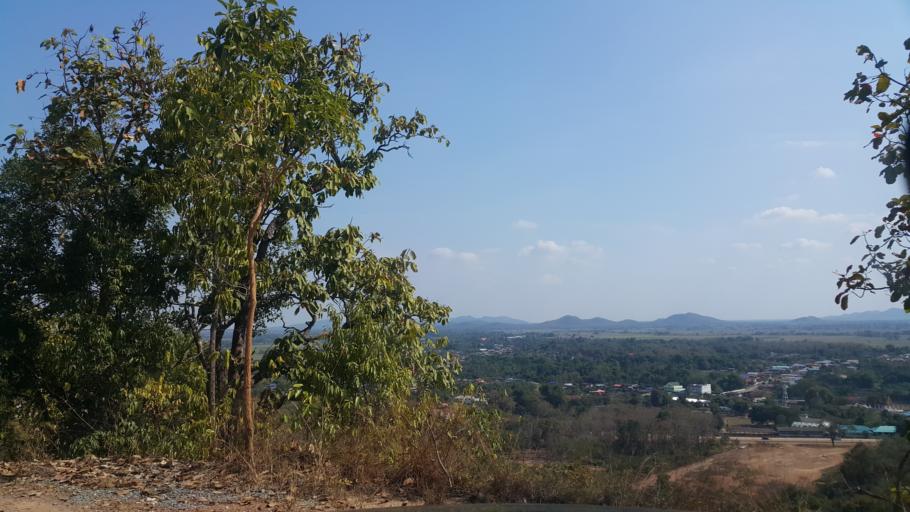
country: TH
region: Sukhothai
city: Thung Saliam
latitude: 17.3423
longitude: 99.5892
